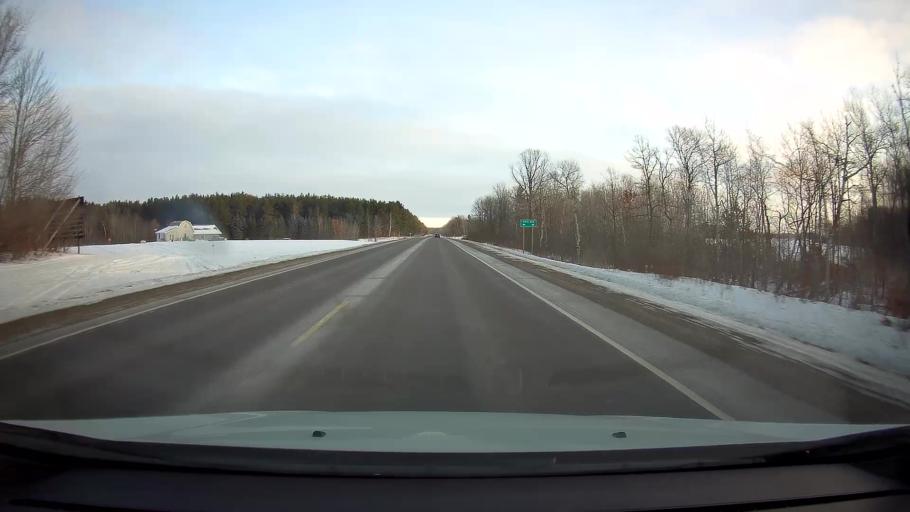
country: US
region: Wisconsin
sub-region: Polk County
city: Clear Lake
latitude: 45.2724
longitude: -92.2444
